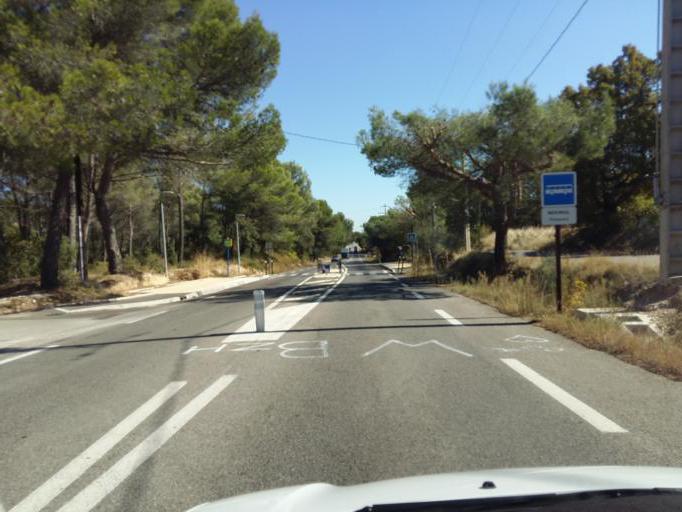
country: FR
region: Provence-Alpes-Cote d'Azur
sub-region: Departement du Vaucluse
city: Merindol
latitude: 43.7531
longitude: 5.1944
